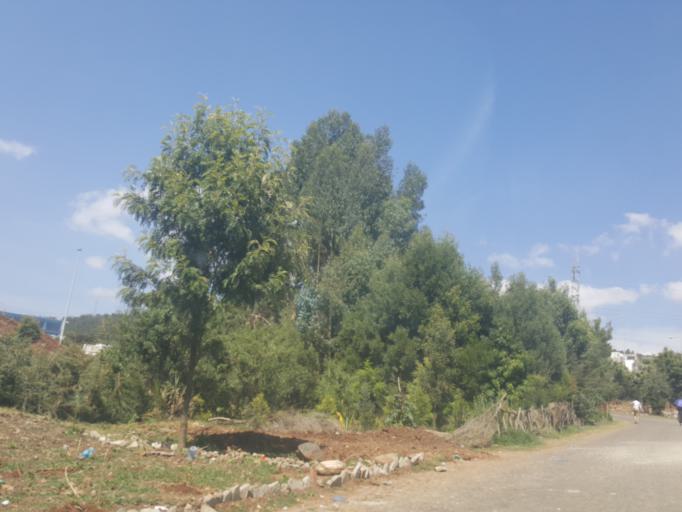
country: ET
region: Adis Abeba
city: Addis Ababa
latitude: 9.0654
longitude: 38.7160
